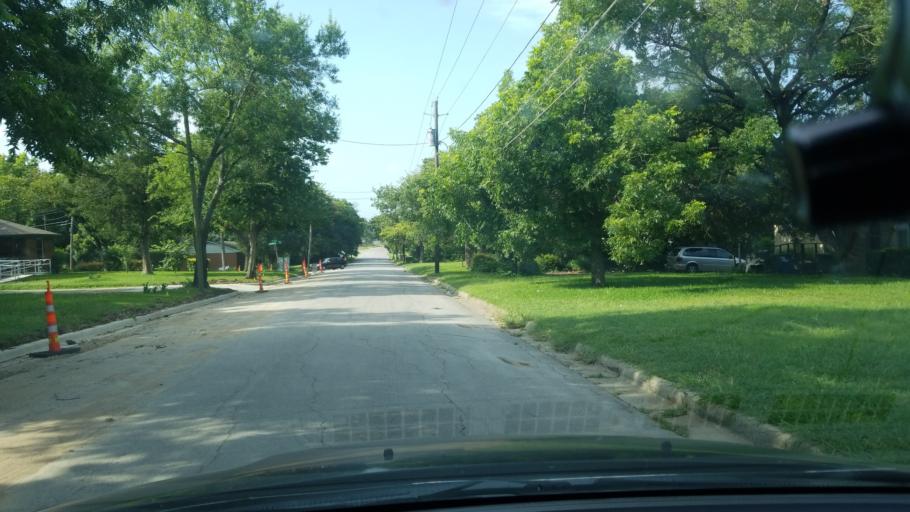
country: US
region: Texas
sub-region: Dallas County
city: Hutchins
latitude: 32.7154
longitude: -96.6930
